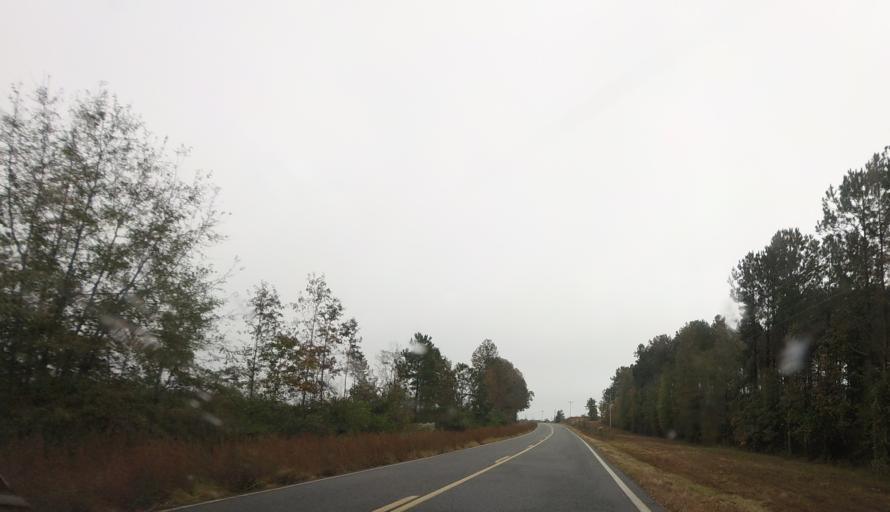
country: US
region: Georgia
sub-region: Taylor County
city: Butler
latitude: 32.4357
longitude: -84.3501
